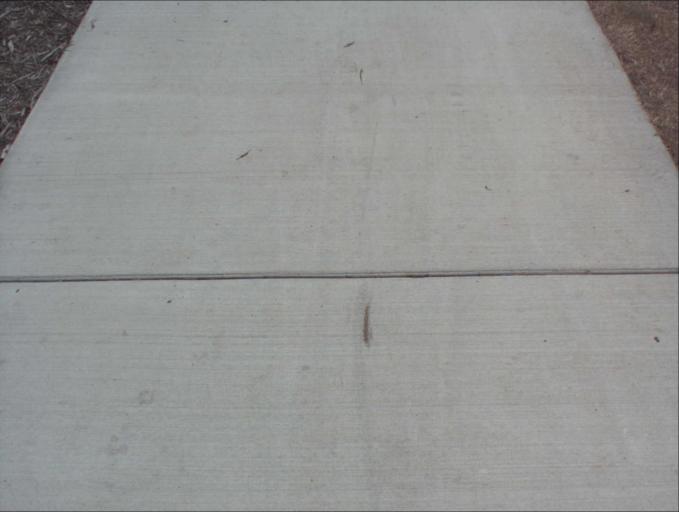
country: AU
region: Queensland
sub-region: Logan
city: North Maclean
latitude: -27.8154
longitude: 152.9664
